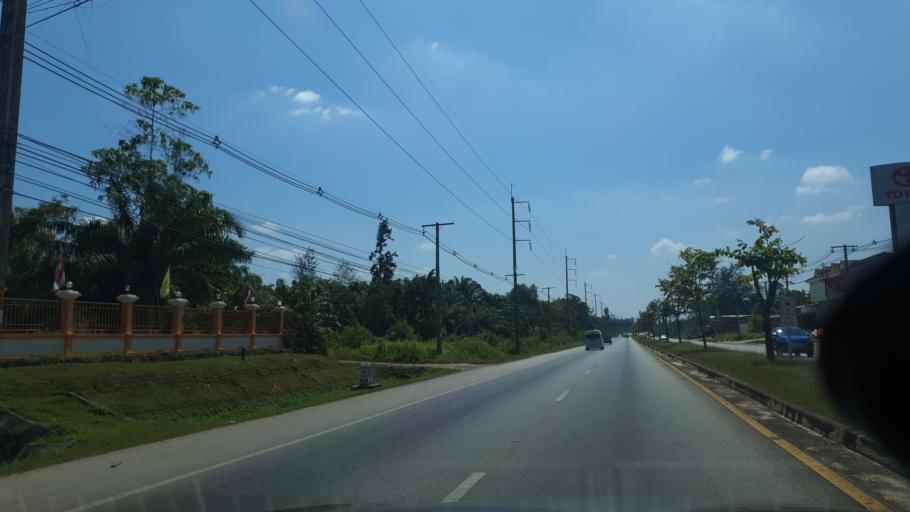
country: TH
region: Krabi
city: Khlong Thom
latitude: 7.9760
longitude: 99.1392
